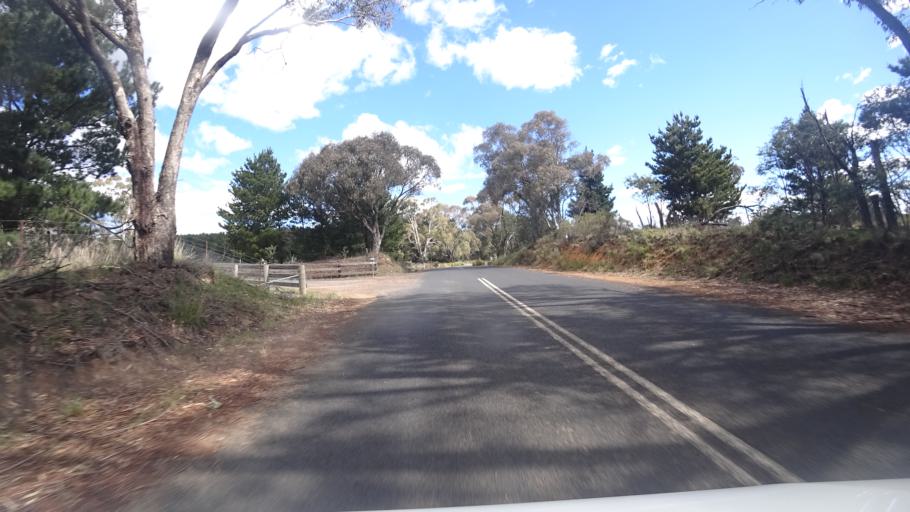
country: AU
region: New South Wales
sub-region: Oberon
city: Oberon
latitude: -33.6828
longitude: 149.7862
